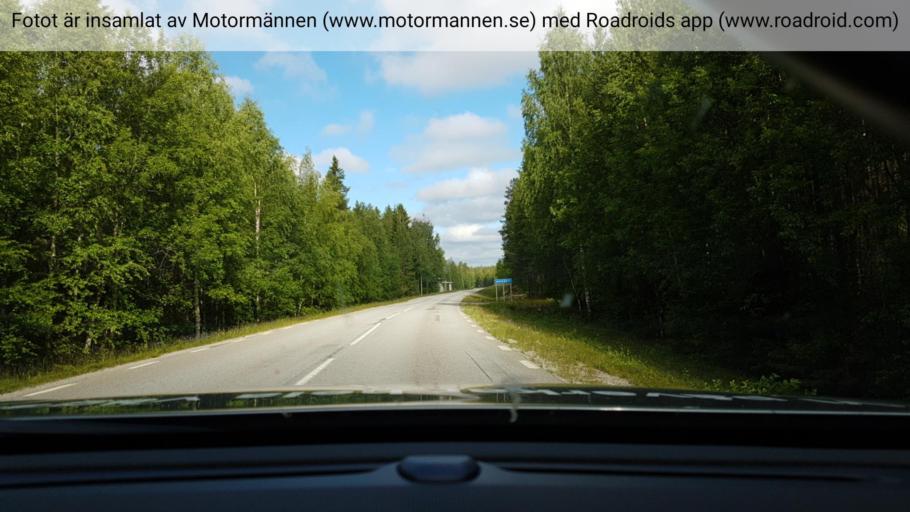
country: SE
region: Vaesterbotten
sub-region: Lycksele Kommun
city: Lycksele
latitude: 64.7745
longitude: 19.0173
